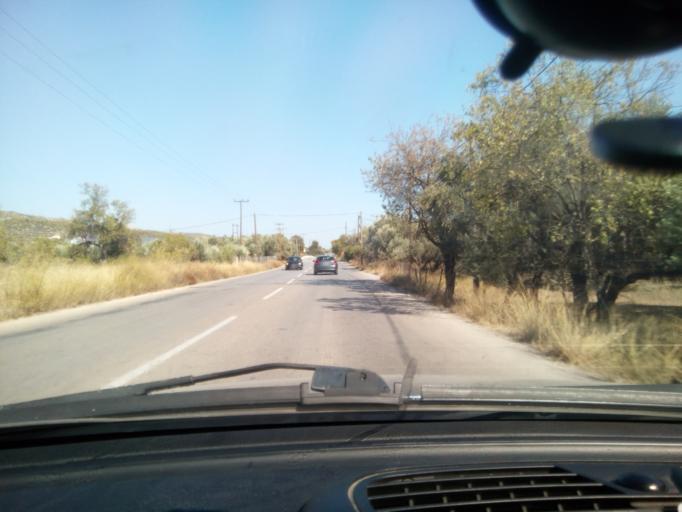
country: GR
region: Central Greece
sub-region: Nomos Evvoias
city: Filla
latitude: 38.4160
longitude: 23.7055
